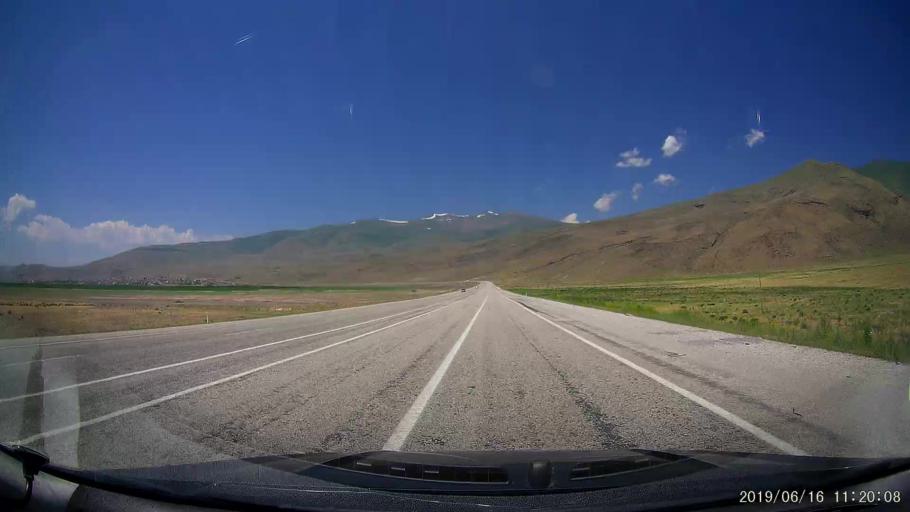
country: TR
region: Agri
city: Dogubayazit
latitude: 39.6972
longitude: 44.0980
